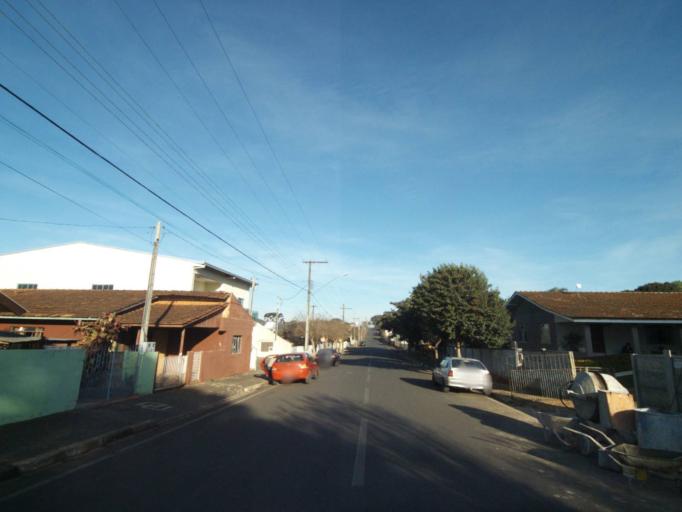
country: BR
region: Parana
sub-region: Tibagi
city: Tibagi
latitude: -24.5179
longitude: -50.4076
